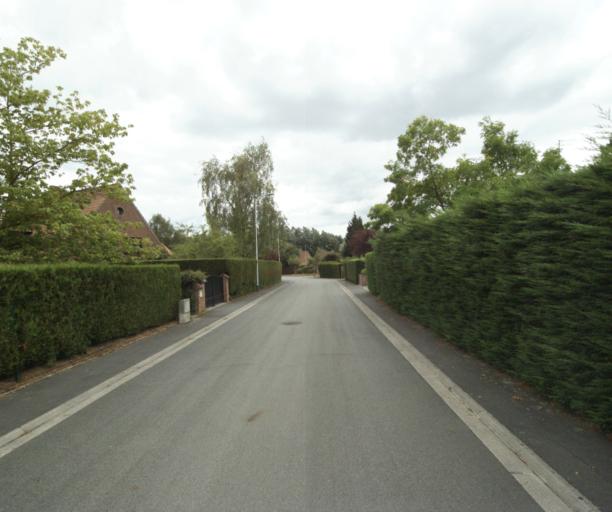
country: FR
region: Nord-Pas-de-Calais
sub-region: Departement du Nord
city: Hem
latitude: 50.6638
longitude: 3.1732
